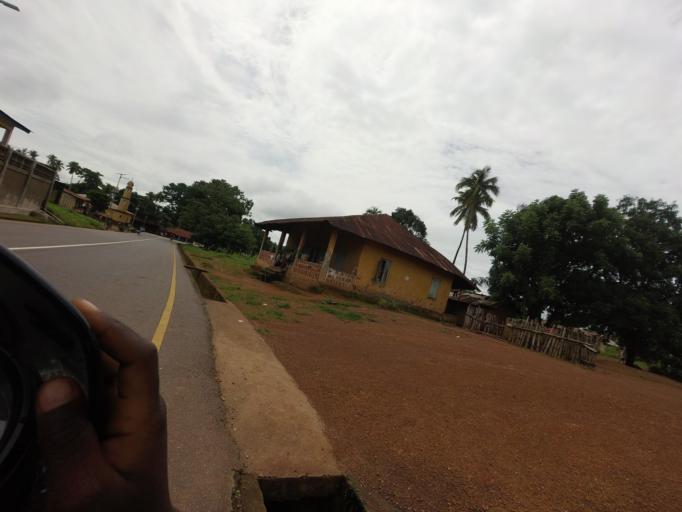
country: SL
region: Northern Province
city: Kambia
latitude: 9.1284
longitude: -12.9194
